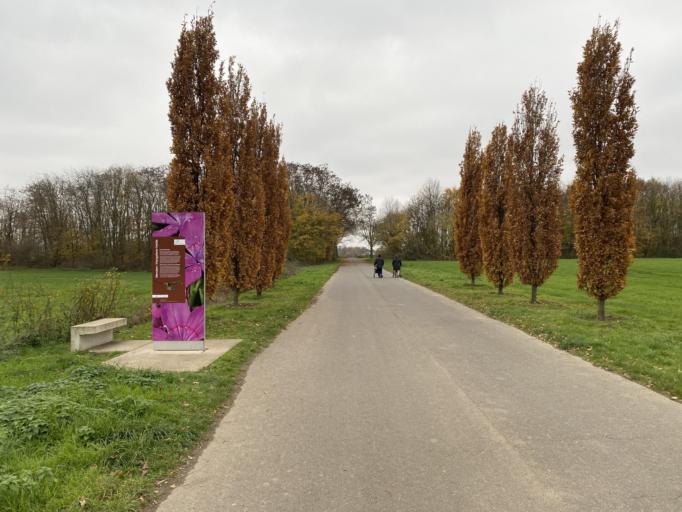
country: DE
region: North Rhine-Westphalia
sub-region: Regierungsbezirk Koln
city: Troisdorf
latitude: 50.7780
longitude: 7.1624
